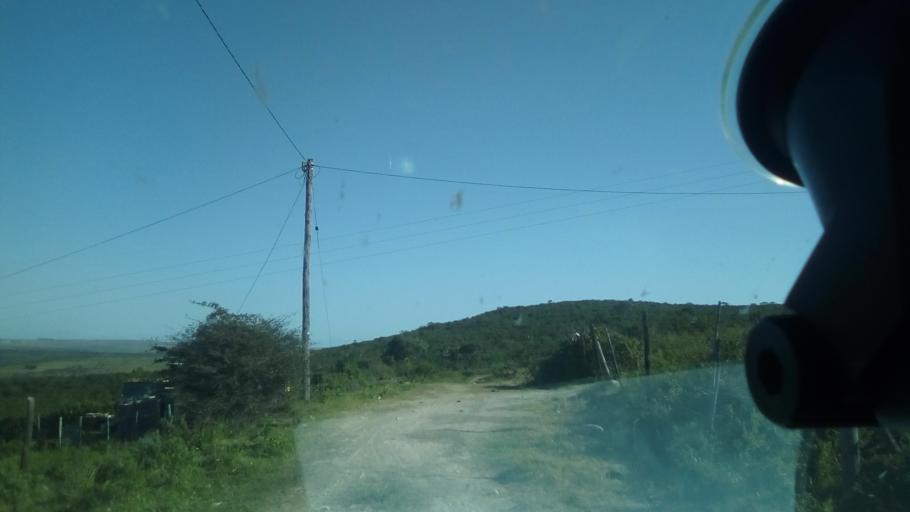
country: ZA
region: Eastern Cape
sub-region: Buffalo City Metropolitan Municipality
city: Bhisho
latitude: -32.8129
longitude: 27.3494
